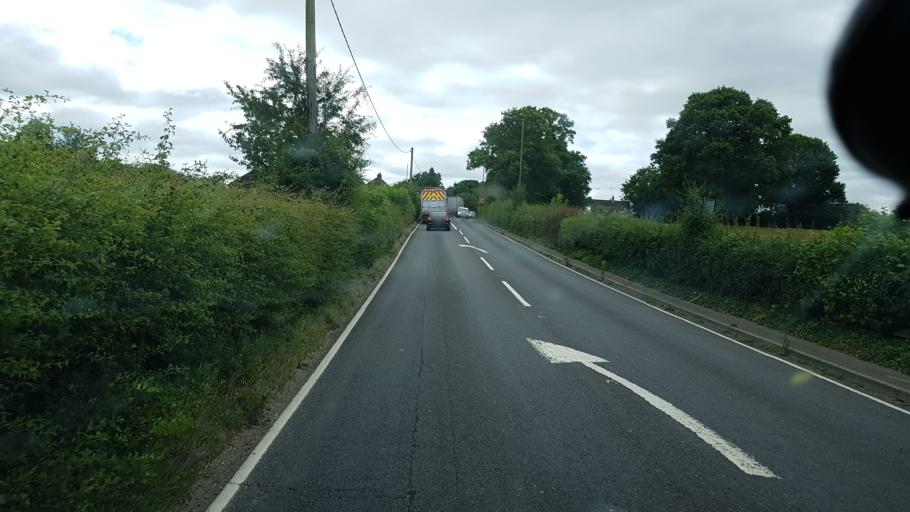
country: GB
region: England
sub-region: Surrey
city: Godstone
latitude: 51.2235
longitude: -0.0470
